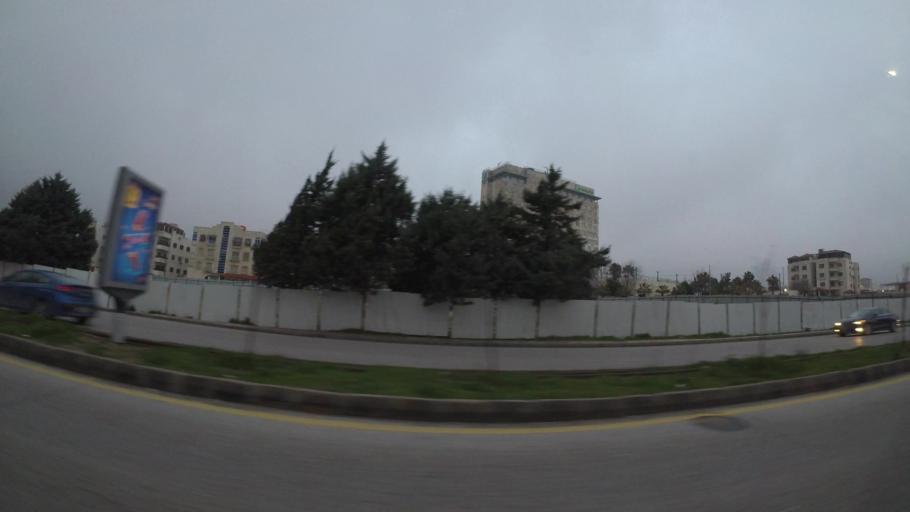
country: JO
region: Amman
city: Al Jubayhah
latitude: 31.9853
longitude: 35.8661
